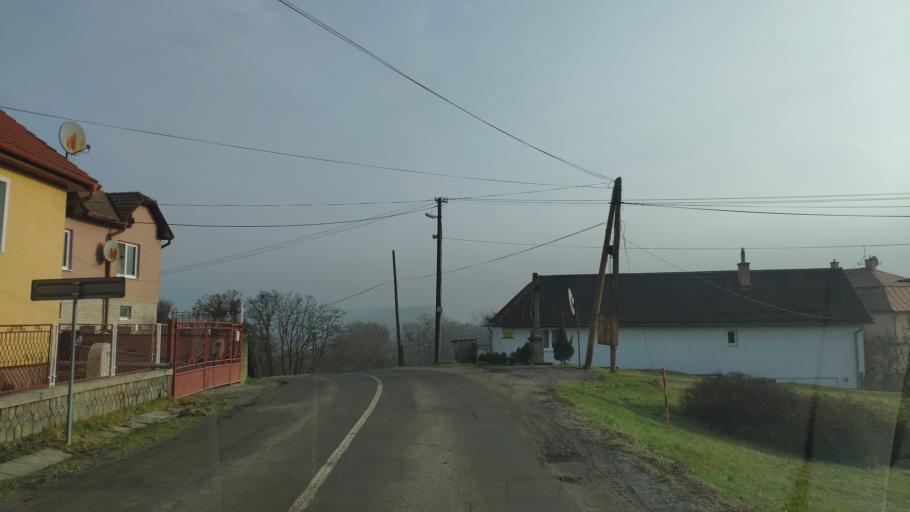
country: SK
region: Kosicky
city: Kosice
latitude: 48.7054
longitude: 21.4117
